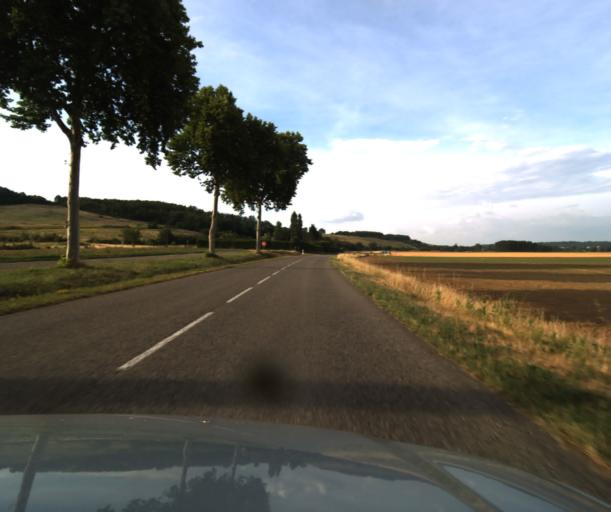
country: FR
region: Midi-Pyrenees
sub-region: Departement du Tarn-et-Garonne
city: Castelsarrasin
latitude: 43.9579
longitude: 1.1031
